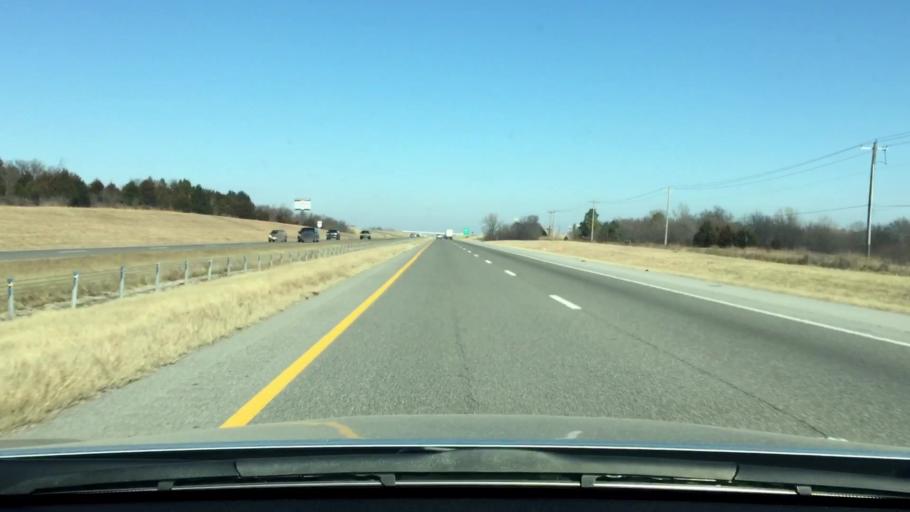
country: US
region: Oklahoma
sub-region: McClain County
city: Purcell
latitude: 34.9731
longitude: -97.3711
